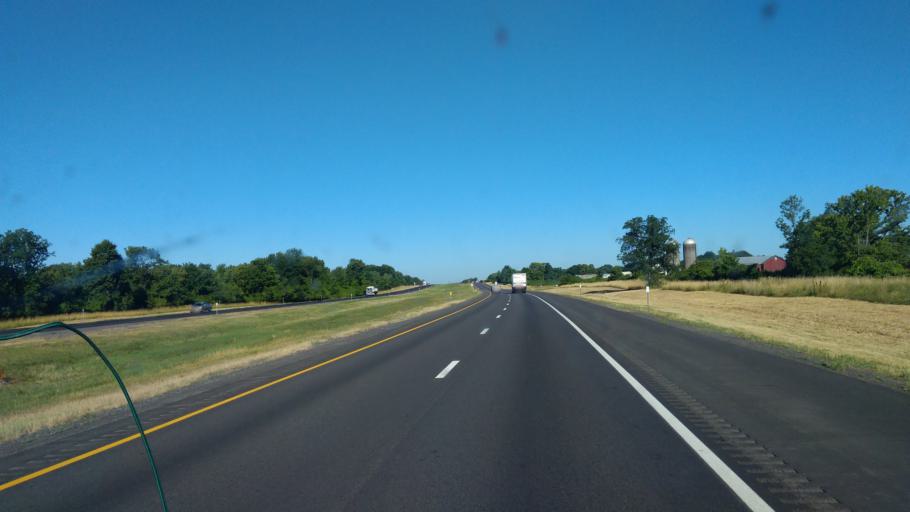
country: US
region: New York
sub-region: Ontario County
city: Phelps
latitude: 42.9744
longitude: -77.0928
